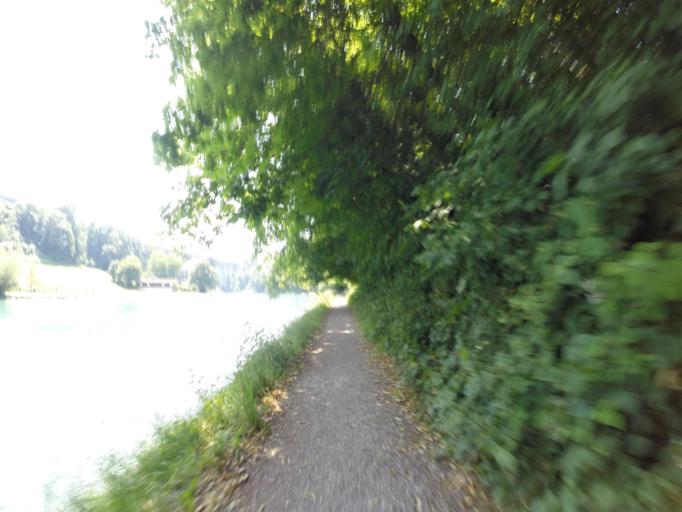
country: CH
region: Bern
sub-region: Bern-Mittelland District
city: Bern
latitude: 46.9576
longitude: 7.4415
